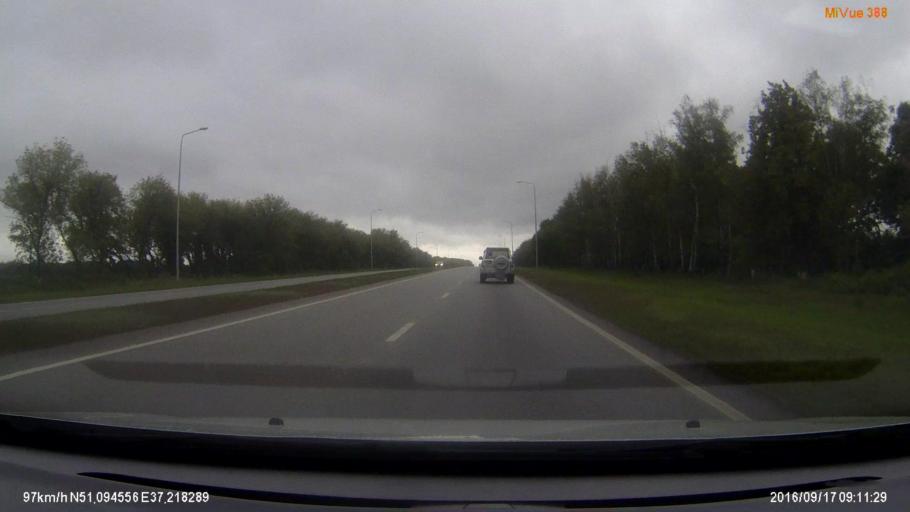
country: RU
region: Belgorod
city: Skorodnoye
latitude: 51.0942
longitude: 37.2181
